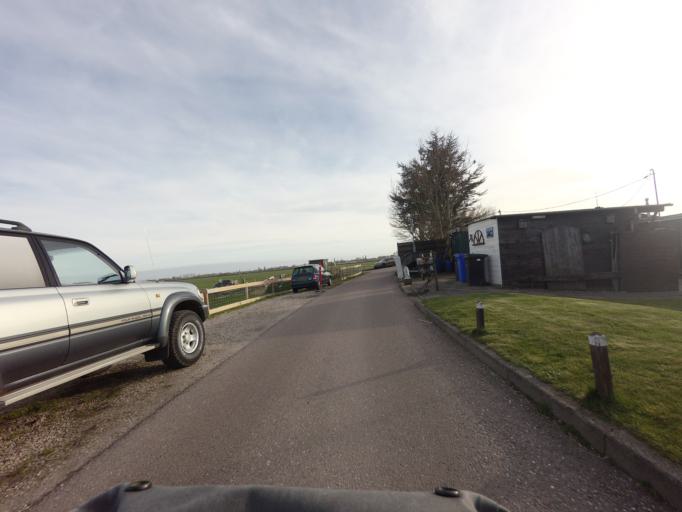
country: NL
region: North Holland
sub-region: Gemeente Weesp
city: Weesp
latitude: 52.3110
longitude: 5.0584
